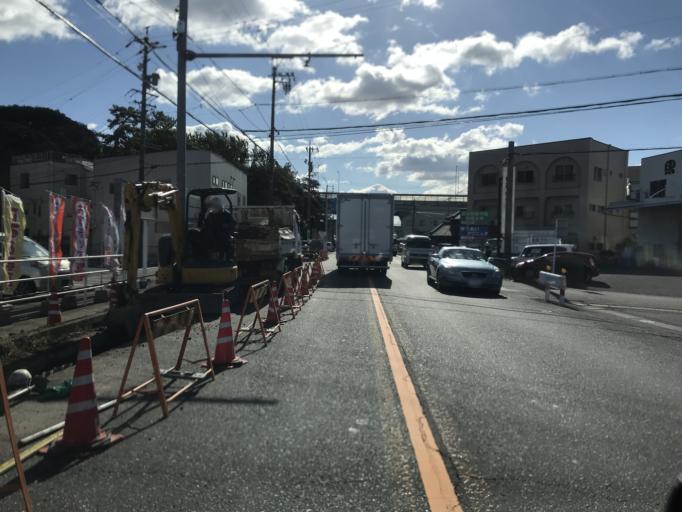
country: JP
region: Aichi
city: Inazawa
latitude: 35.2220
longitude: 136.8419
